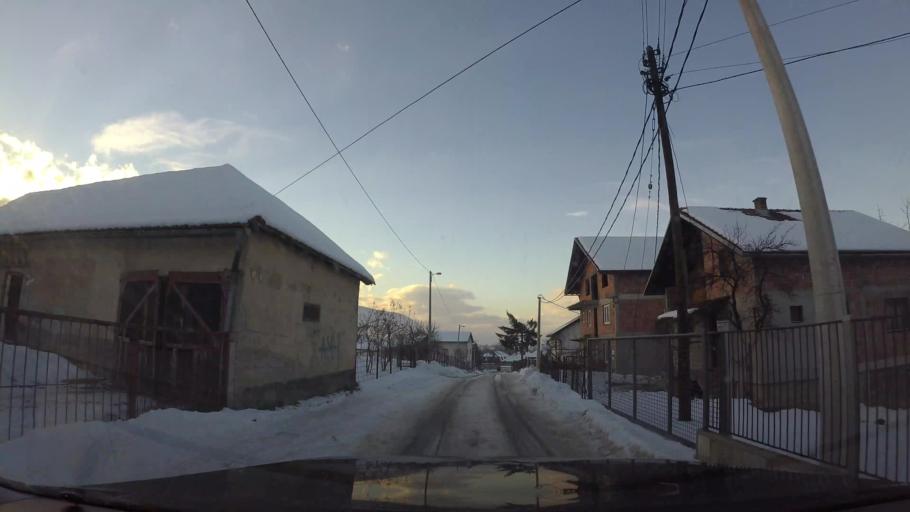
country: BA
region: Federation of Bosnia and Herzegovina
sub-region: Kanton Sarajevo
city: Sarajevo
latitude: 43.8113
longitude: 18.3525
